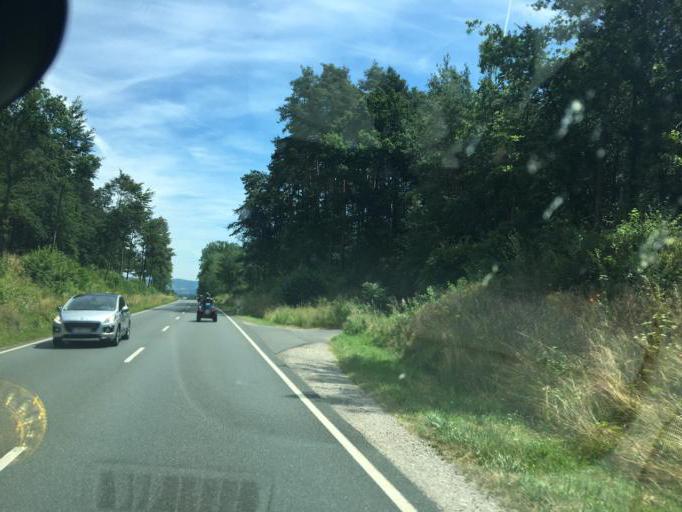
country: DE
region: Bavaria
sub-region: Upper Franconia
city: Hausen
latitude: 49.7025
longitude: 11.0277
